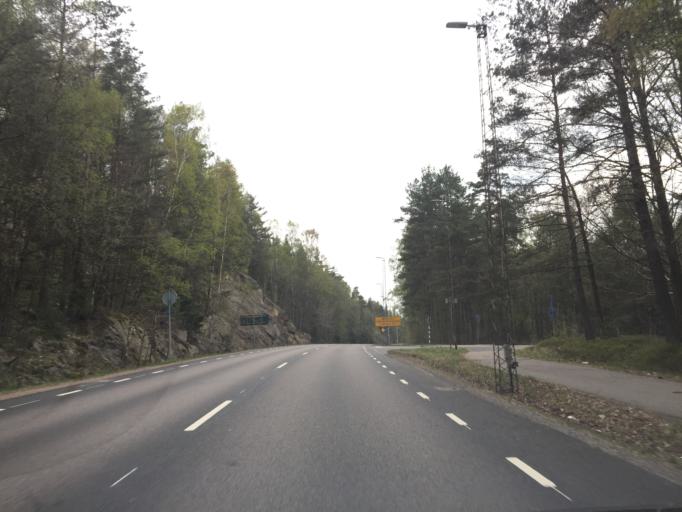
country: SE
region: Vaestra Goetaland
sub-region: Goteborg
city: Rannebergen
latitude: 57.8053
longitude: 12.0604
